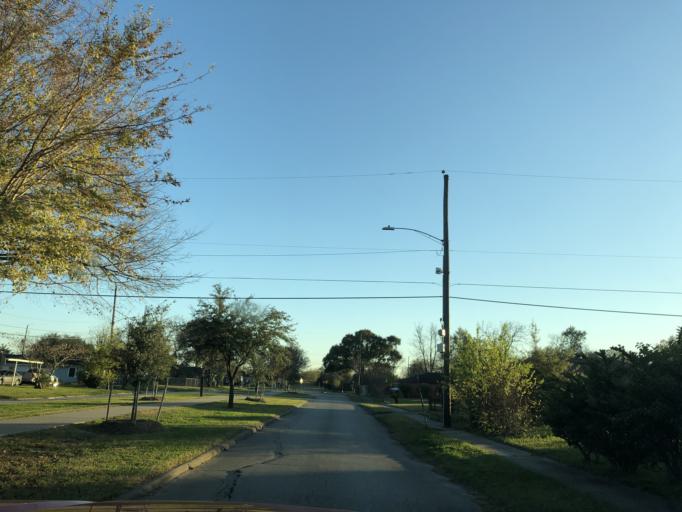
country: US
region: Texas
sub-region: Harris County
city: Jacinto City
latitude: 29.7617
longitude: -95.2701
